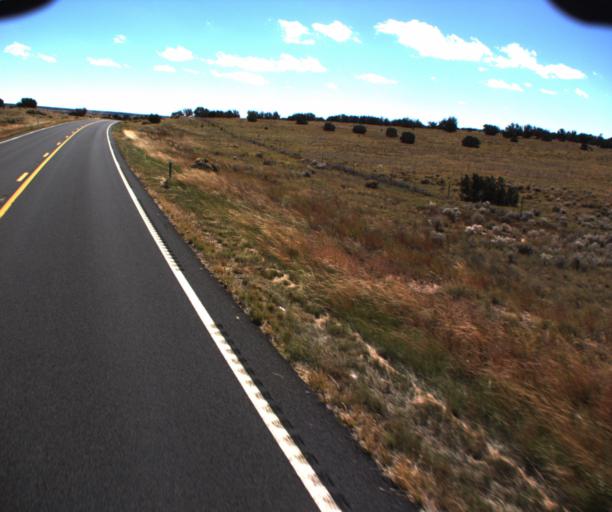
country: US
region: Arizona
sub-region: Apache County
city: Houck
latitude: 35.0280
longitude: -109.2491
